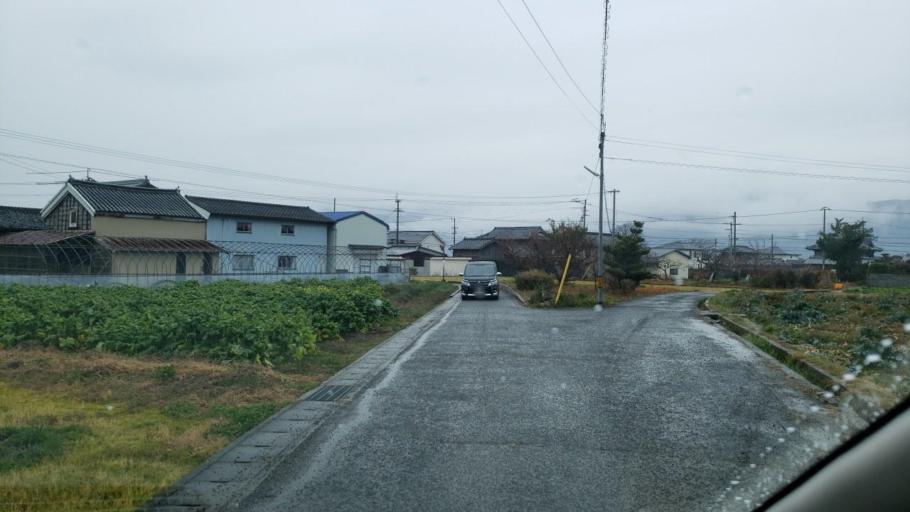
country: JP
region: Tokushima
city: Kamojimacho-jogejima
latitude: 34.0816
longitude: 134.2574
